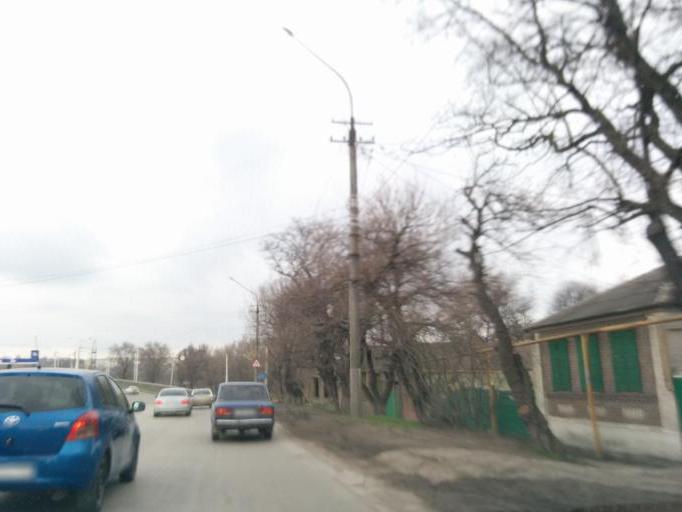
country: RU
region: Rostov
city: Novocherkassk
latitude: 47.4379
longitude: 40.1000
